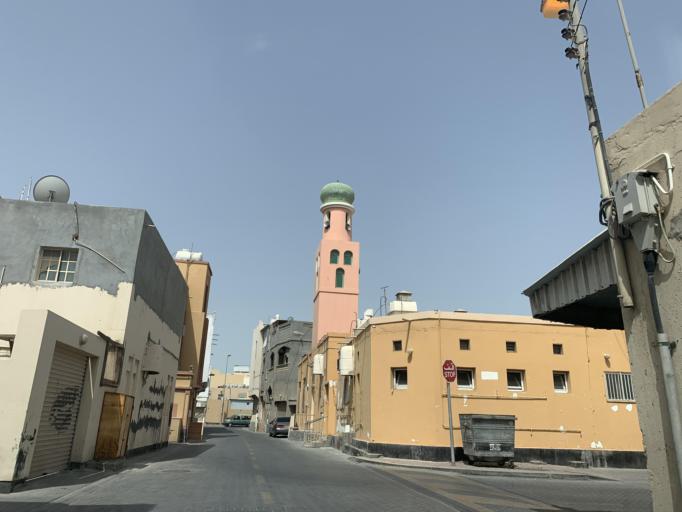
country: BH
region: Northern
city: Sitrah
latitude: 26.1343
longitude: 50.6003
